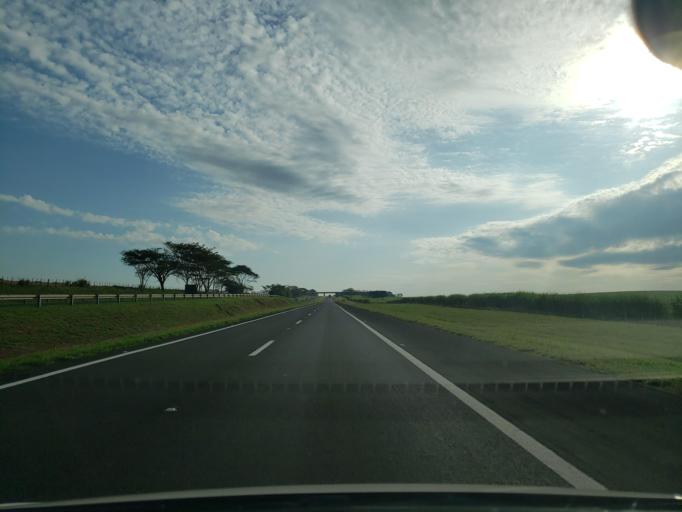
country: BR
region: Sao Paulo
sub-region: Valparaiso
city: Valparaiso
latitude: -21.2055
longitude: -50.7837
